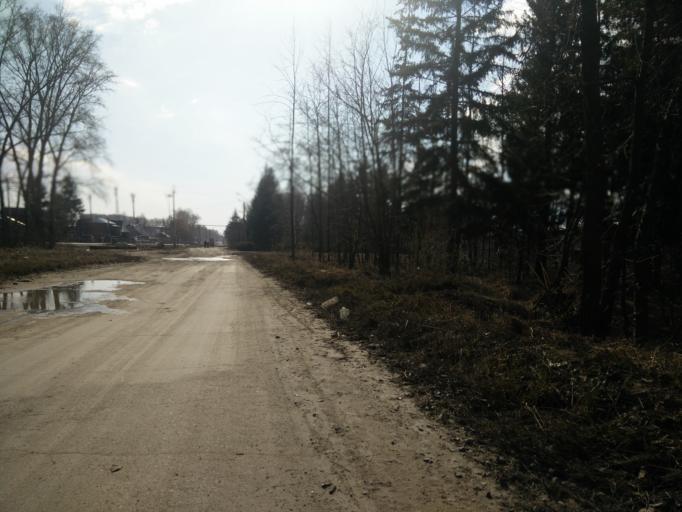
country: RU
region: Novosibirsk
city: Berdsk
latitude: 54.7597
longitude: 83.0682
